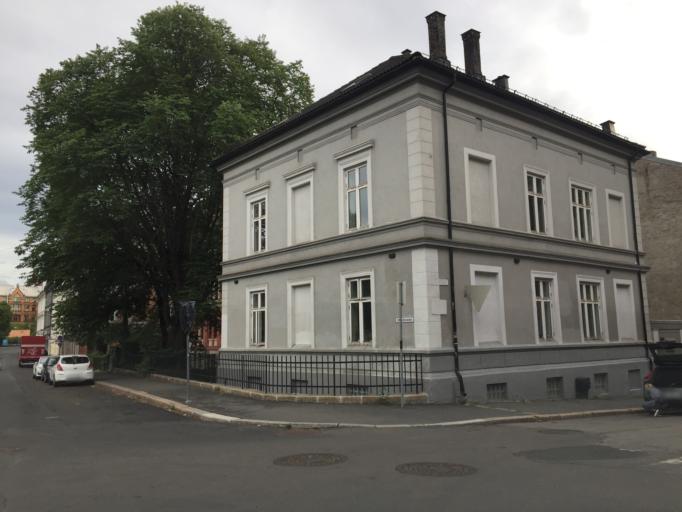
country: NO
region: Oslo
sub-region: Oslo
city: Oslo
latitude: 59.9212
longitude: 10.7419
